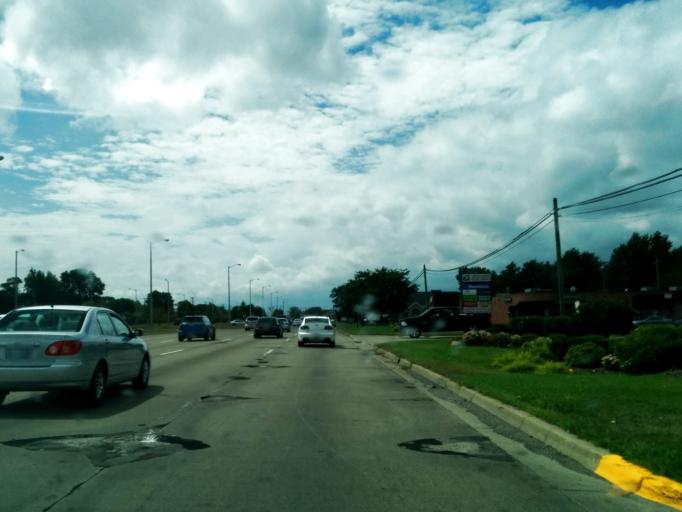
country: US
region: Michigan
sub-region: Macomb County
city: Utica
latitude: 42.6261
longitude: -83.0227
